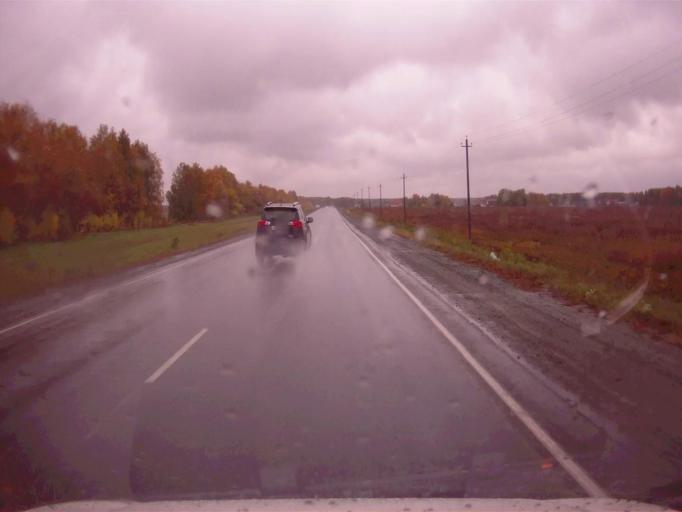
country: RU
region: Chelyabinsk
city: Argayash
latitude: 55.4040
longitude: 61.0645
